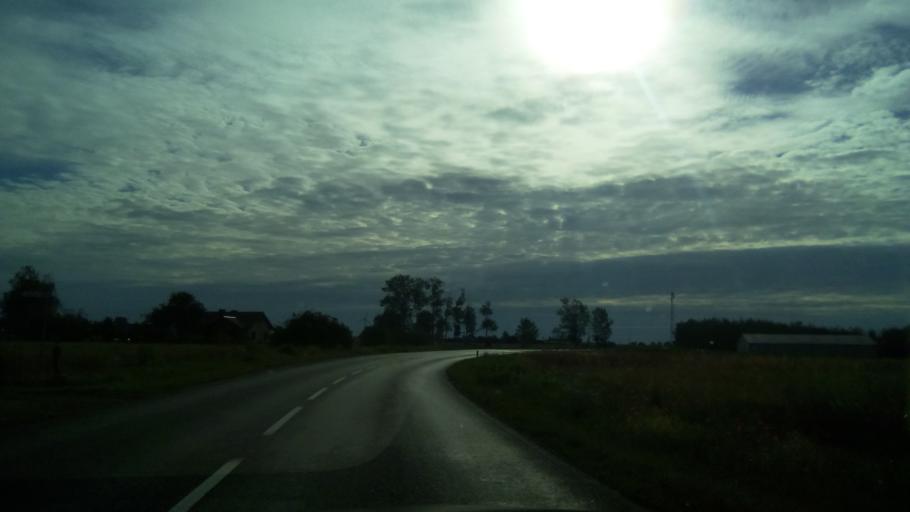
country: PL
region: Greater Poland Voivodeship
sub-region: Powiat koninski
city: Rzgow Pierwszy
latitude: 52.2033
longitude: 18.0127
